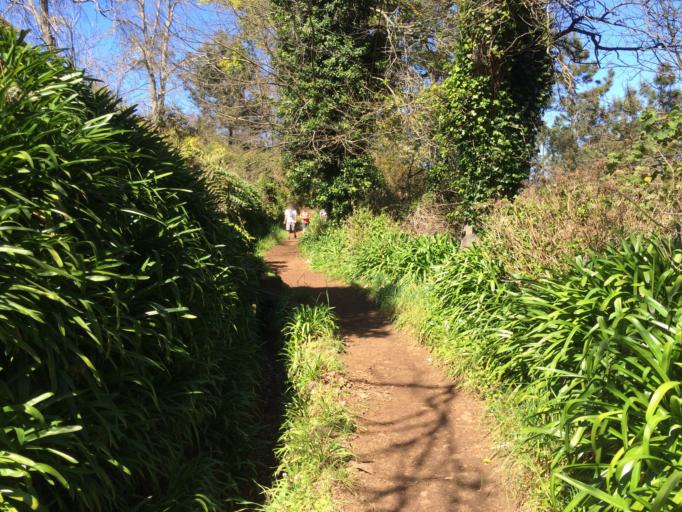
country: PT
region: Madeira
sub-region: Santa Cruz
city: Camacha
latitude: 32.6792
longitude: -16.8551
